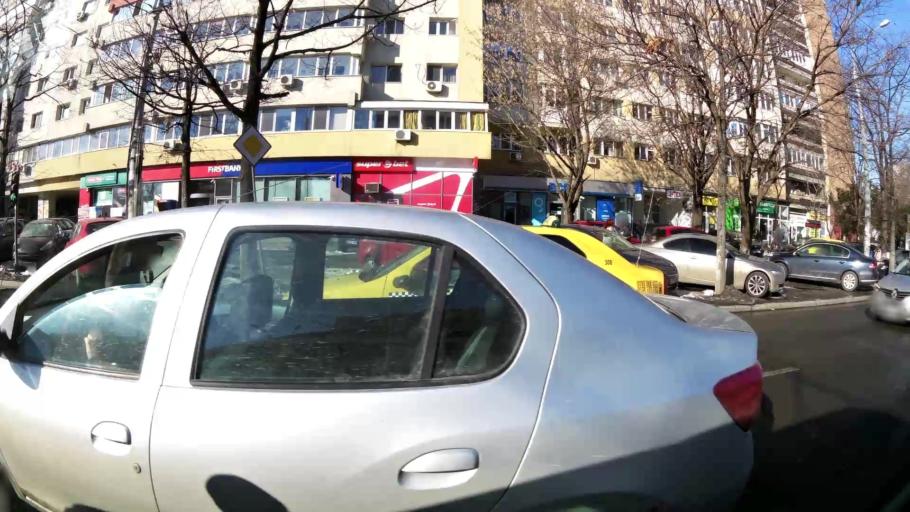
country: RO
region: Bucuresti
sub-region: Municipiul Bucuresti
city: Bucharest
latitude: 44.4555
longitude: 26.1289
